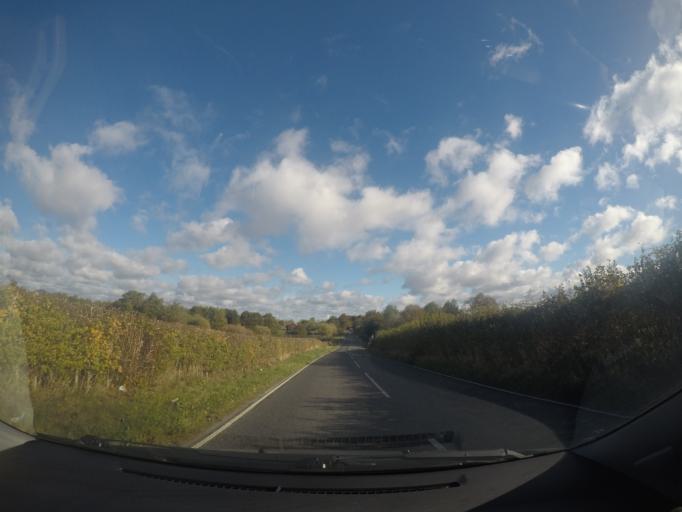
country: GB
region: England
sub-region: City and Borough of Leeds
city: Walton
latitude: 54.0249
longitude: -1.3046
